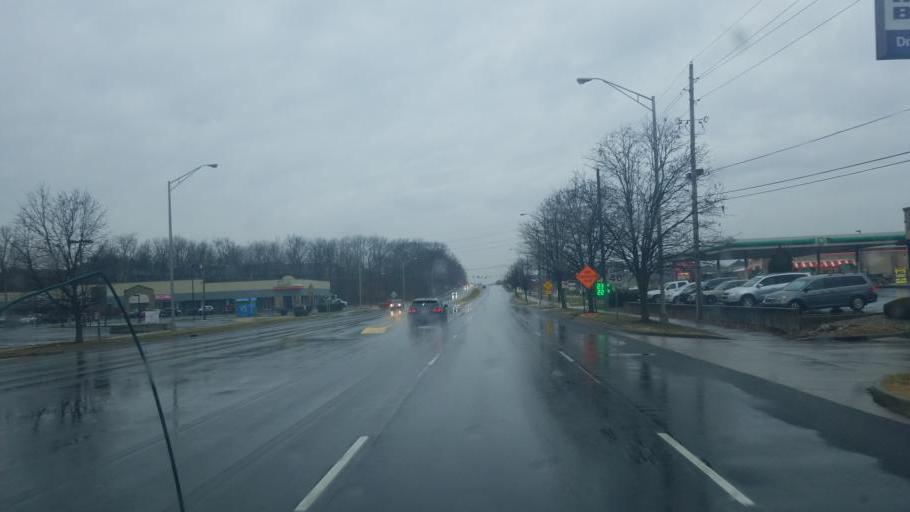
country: US
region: Indiana
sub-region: Bartholomew County
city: Columbus
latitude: 39.2002
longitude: -85.9622
